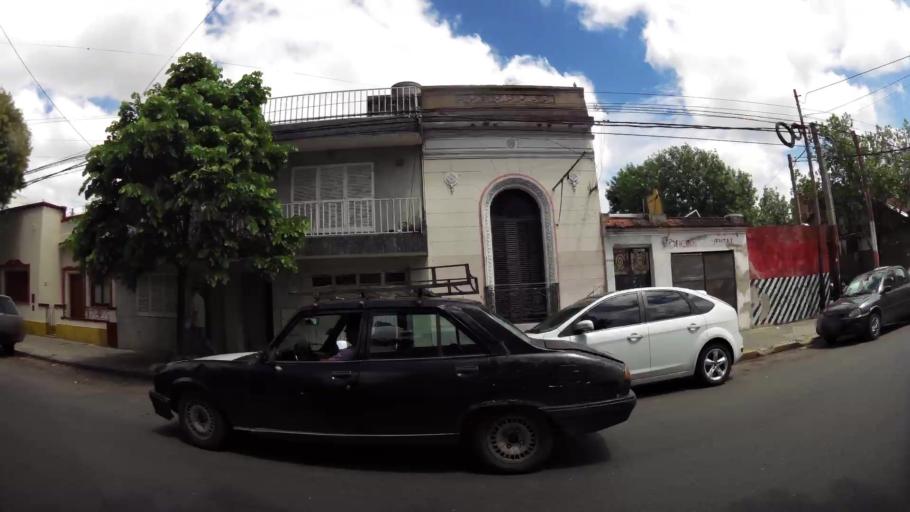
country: AR
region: Santa Fe
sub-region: Departamento de Rosario
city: Rosario
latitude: -32.9639
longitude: -60.6322
